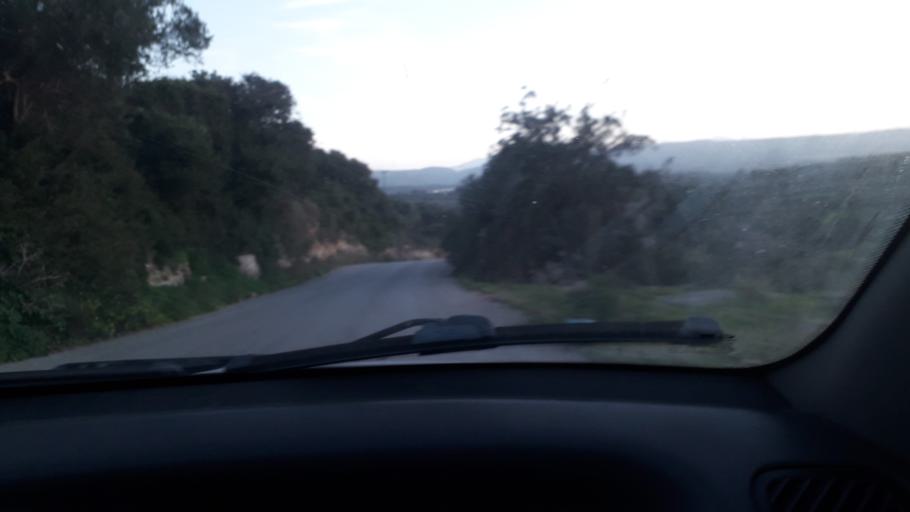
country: GR
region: Crete
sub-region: Nomos Rethymnis
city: Panormos
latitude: 35.3834
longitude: 24.6237
